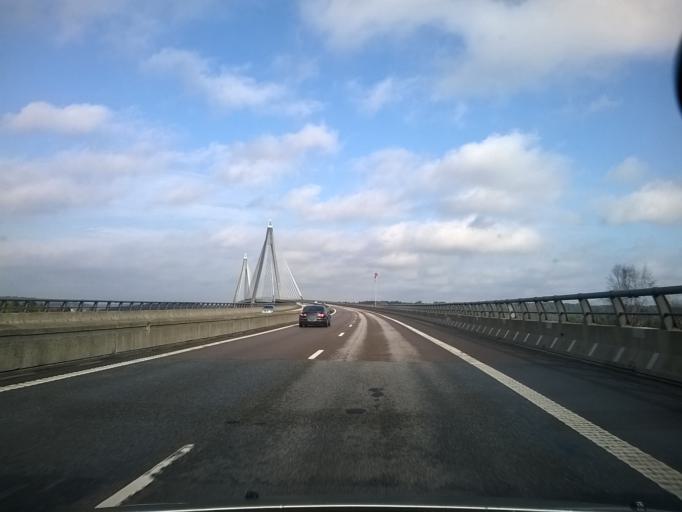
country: SE
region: Vaestra Goetaland
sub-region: Uddevalla Kommun
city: Uddevalla
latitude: 58.3200
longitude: 11.8546
